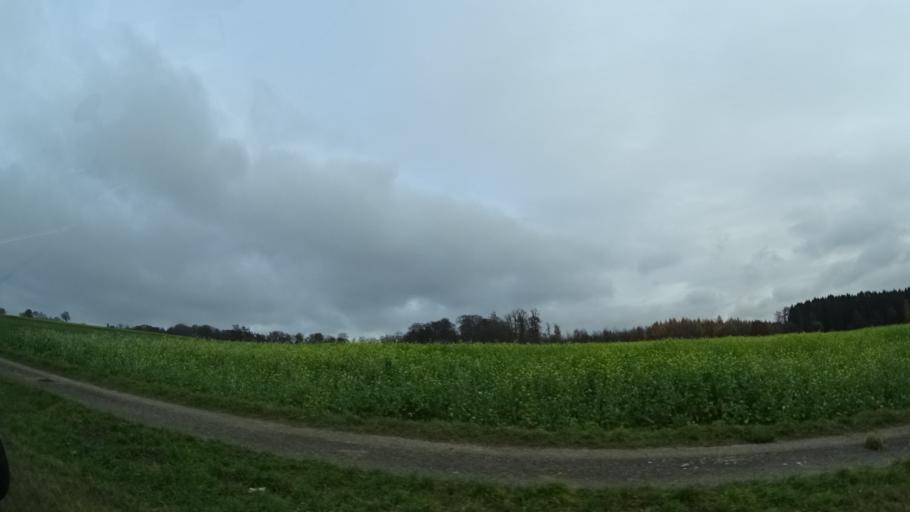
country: DE
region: Baden-Wuerttemberg
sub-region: Karlsruhe Region
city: Neckargerach
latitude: 49.4232
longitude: 9.0858
